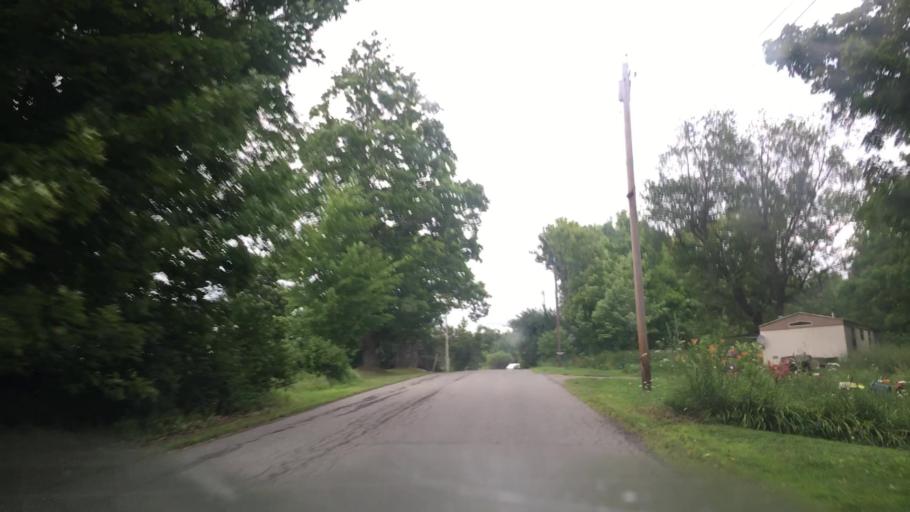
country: US
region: Maine
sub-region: Penobscot County
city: Veazie
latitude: 44.8486
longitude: -68.7465
